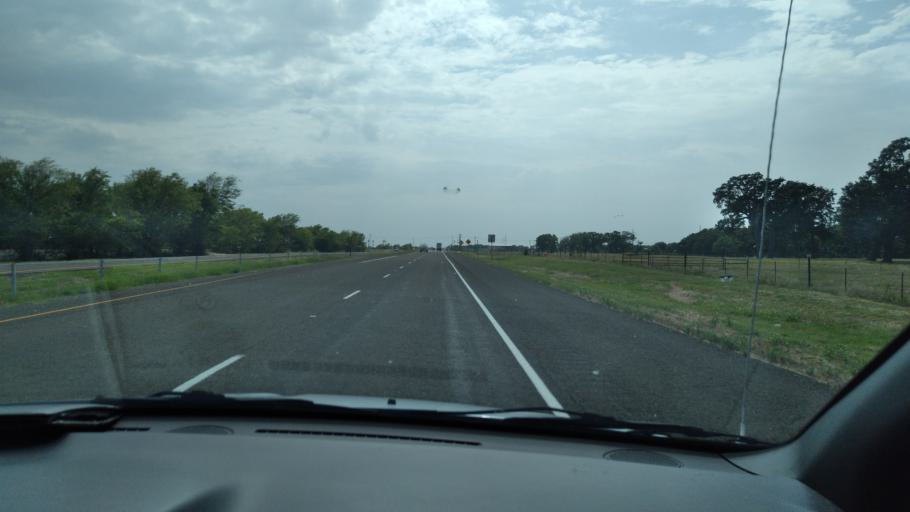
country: US
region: Texas
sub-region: Navarro County
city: Kerens
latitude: 32.1231
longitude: -96.2904
